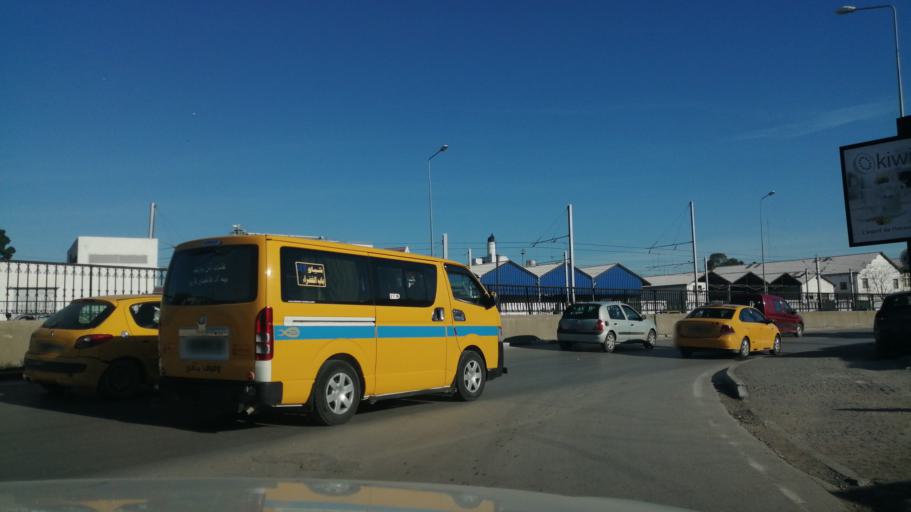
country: TN
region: Tunis
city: Tunis
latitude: 36.8087
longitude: 10.1597
